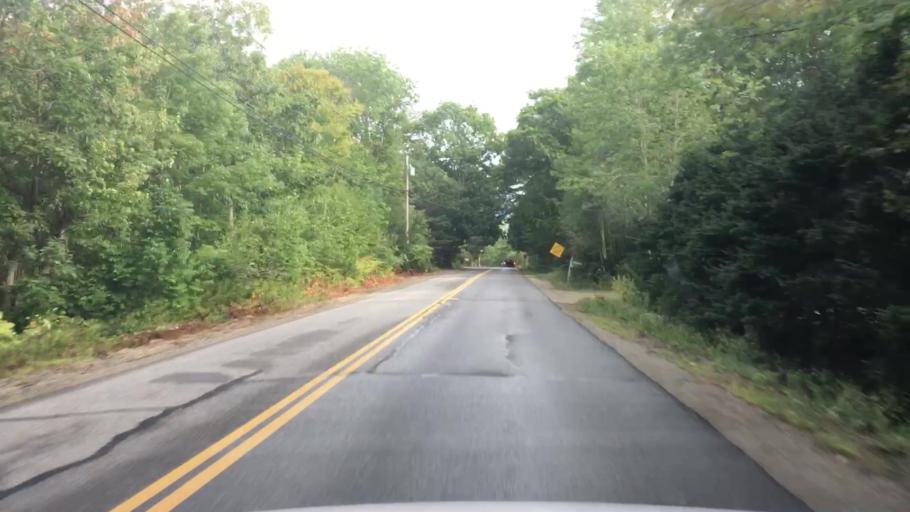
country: US
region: Maine
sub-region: Hancock County
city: Trenton
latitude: 44.4367
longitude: -68.3992
